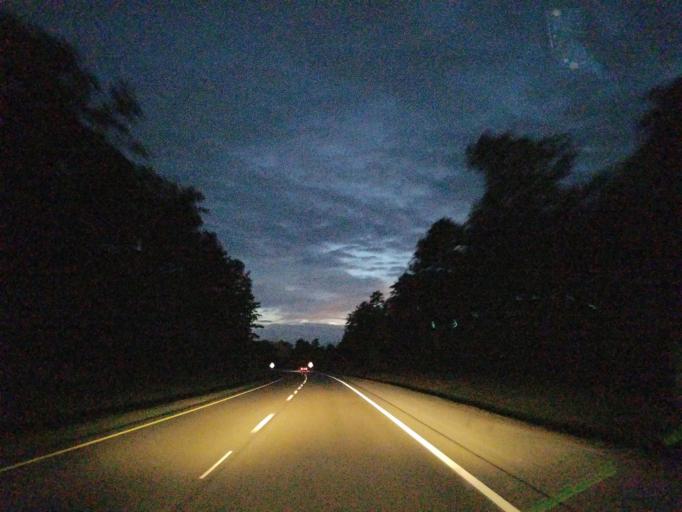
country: US
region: Mississippi
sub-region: Jones County
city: Laurel
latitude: 31.7308
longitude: -89.0980
